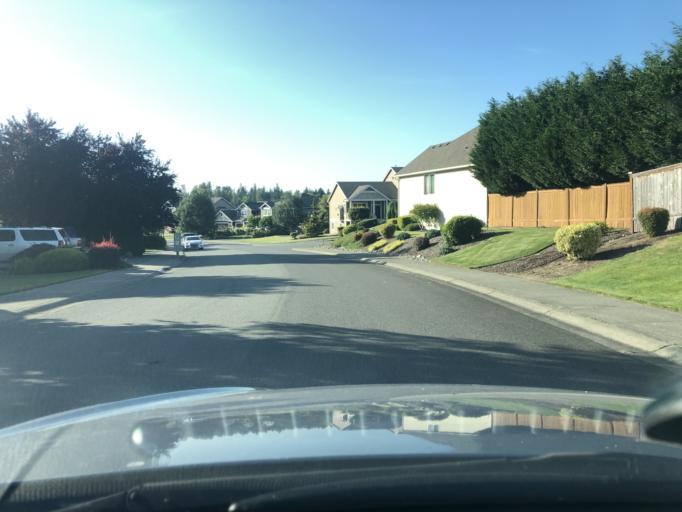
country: US
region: Washington
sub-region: Pierce County
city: Bonney Lake
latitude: 47.2315
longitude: -122.1405
